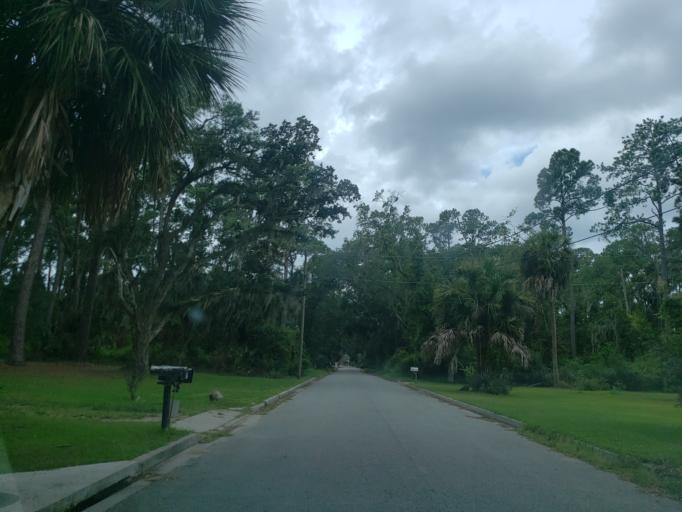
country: US
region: Georgia
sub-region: Chatham County
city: Wilmington Island
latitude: 32.0175
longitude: -80.9516
